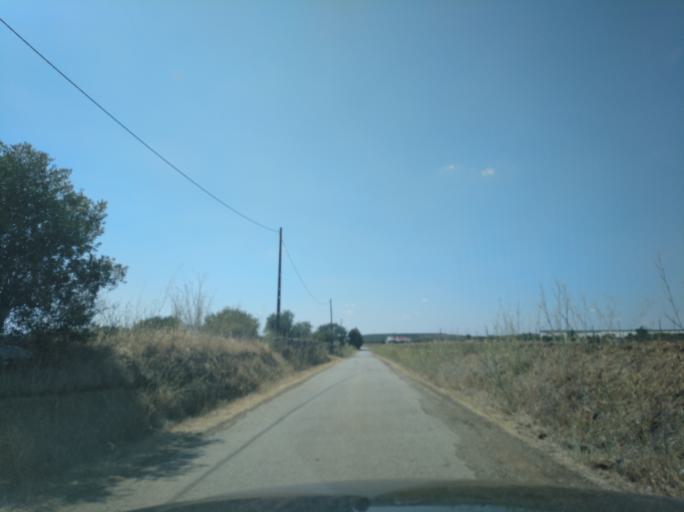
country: PT
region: Portalegre
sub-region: Campo Maior
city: Campo Maior
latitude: 39.0234
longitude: -7.0869
